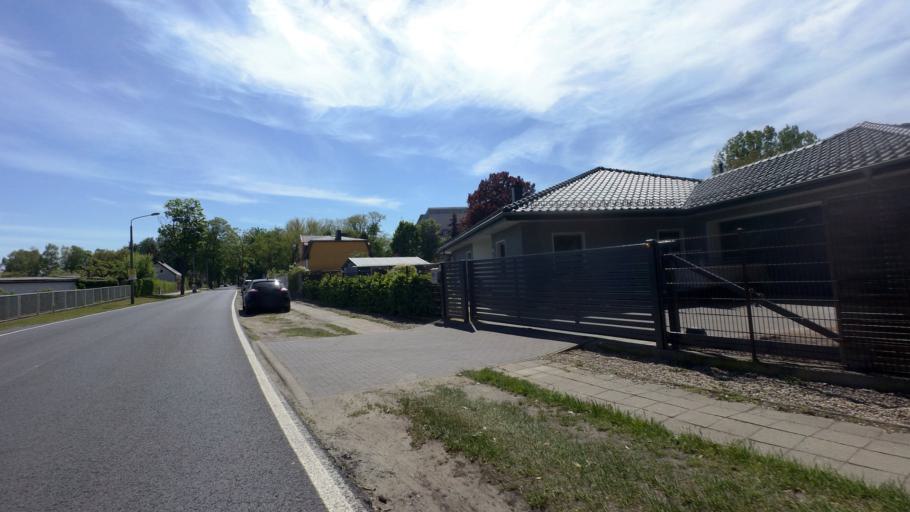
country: DE
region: Brandenburg
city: Luckenwalde
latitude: 52.1041
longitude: 13.1538
